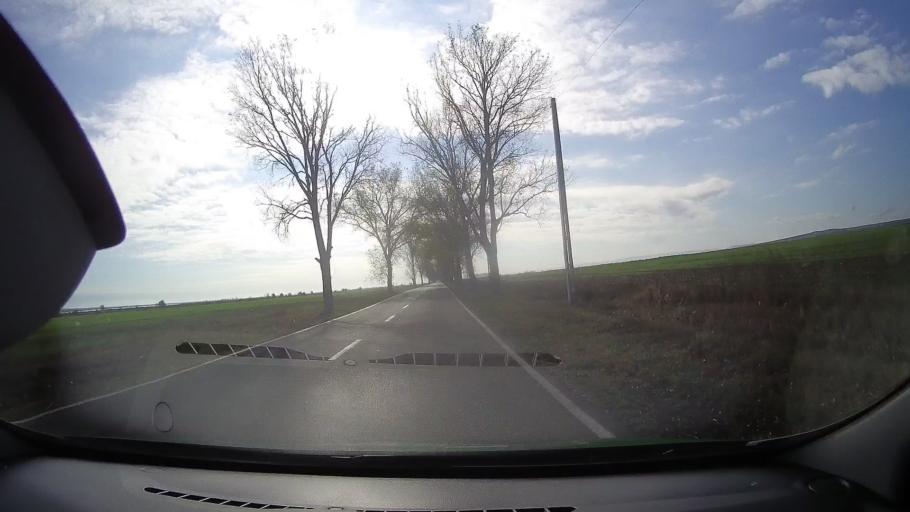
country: RO
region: Tulcea
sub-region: Comuna Valea Nucarilor
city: Agighiol
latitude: 45.0127
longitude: 28.8840
